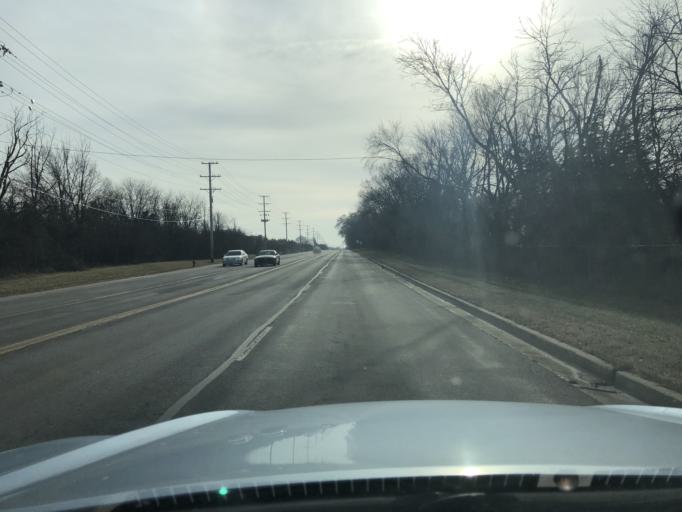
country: US
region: Illinois
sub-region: DuPage County
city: Itasca
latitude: 41.9782
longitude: -87.9982
